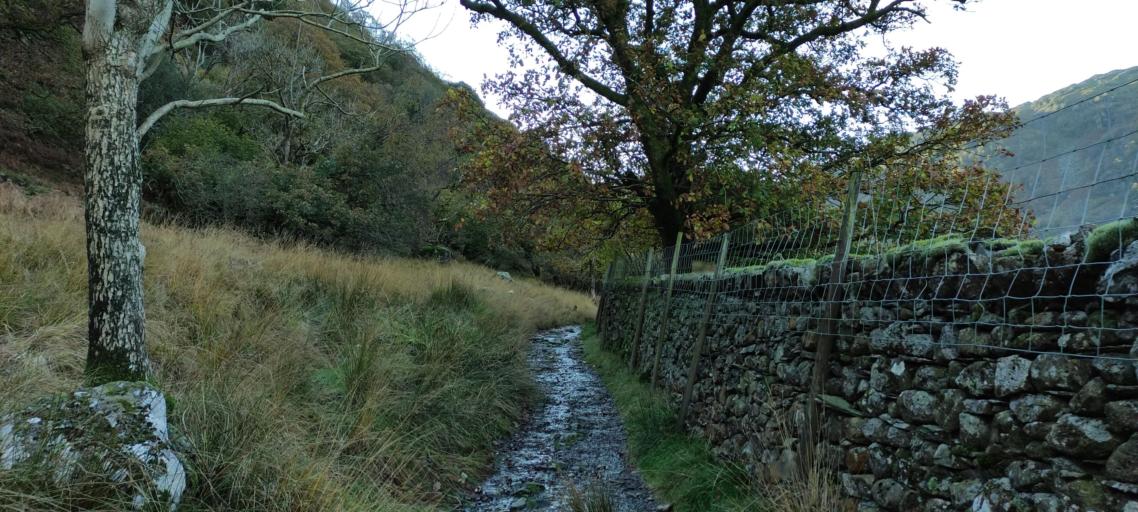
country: GB
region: England
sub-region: Cumbria
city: Keswick
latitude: 54.5204
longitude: -3.1428
